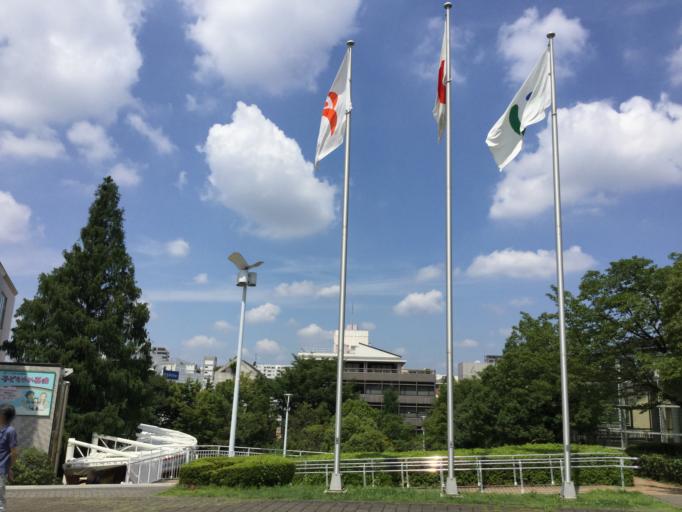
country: JP
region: Tokyo
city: Tokyo
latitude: 35.6754
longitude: 139.6933
